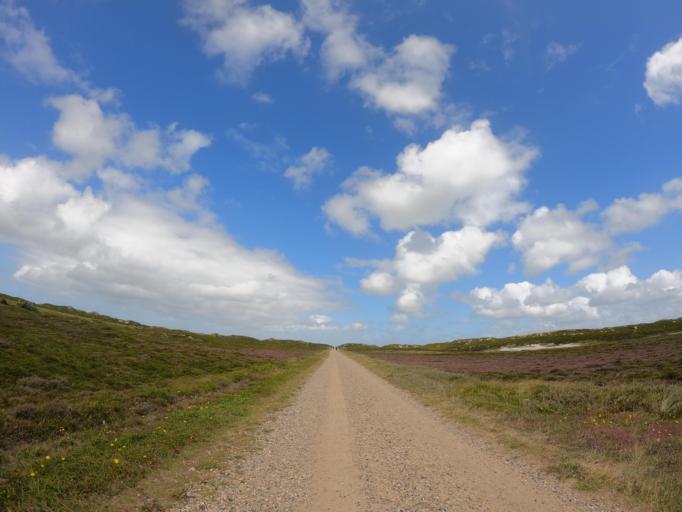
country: DE
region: Schleswig-Holstein
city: Westerland
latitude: 54.8172
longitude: 8.2922
